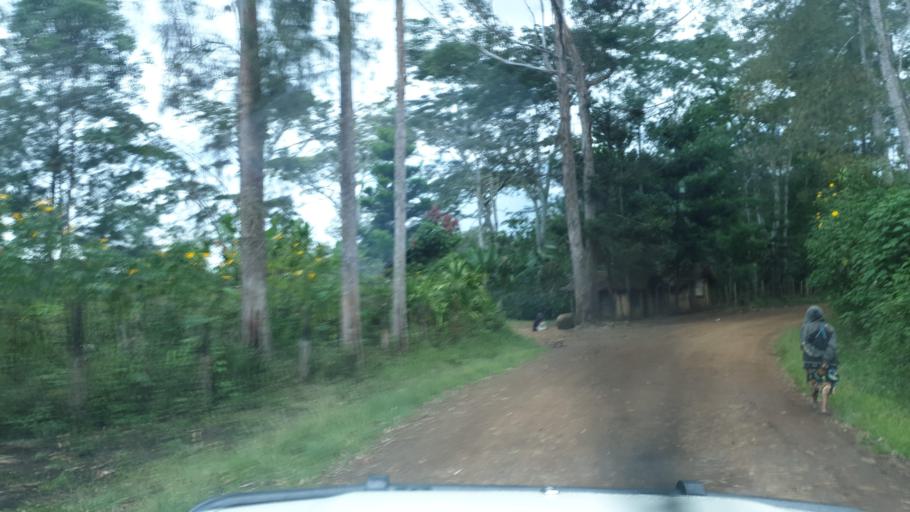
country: PG
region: Eastern Highlands
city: Goroka
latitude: -5.9695
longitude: 145.2772
